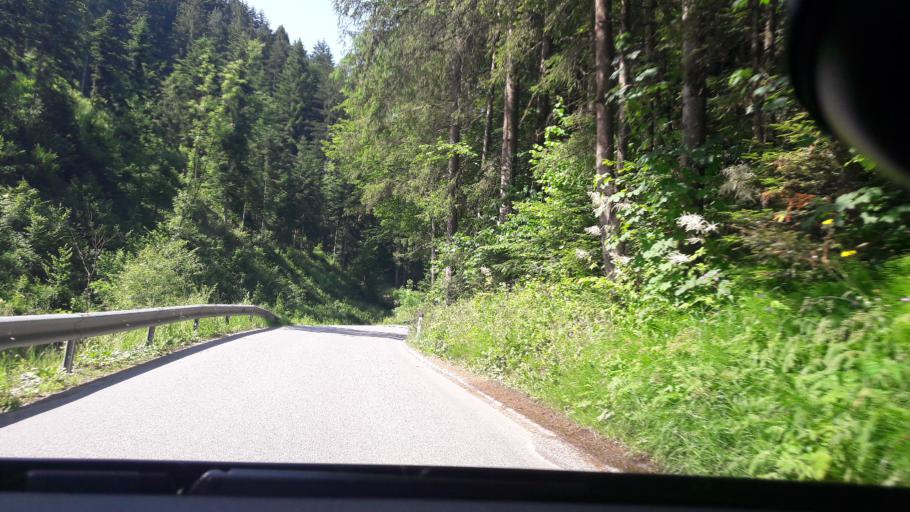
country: AT
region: Styria
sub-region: Politischer Bezirk Voitsberg
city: Kohlschwarz
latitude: 47.1128
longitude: 15.1292
